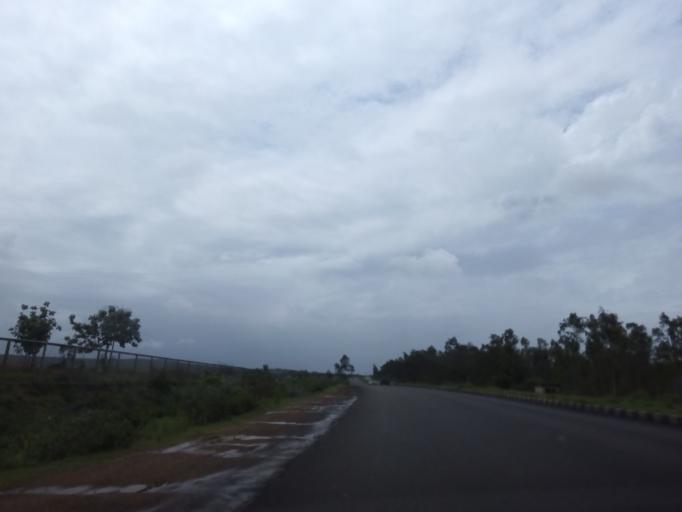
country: IN
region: Karnataka
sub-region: Haveri
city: Byadgi
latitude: 14.7117
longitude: 75.5045
